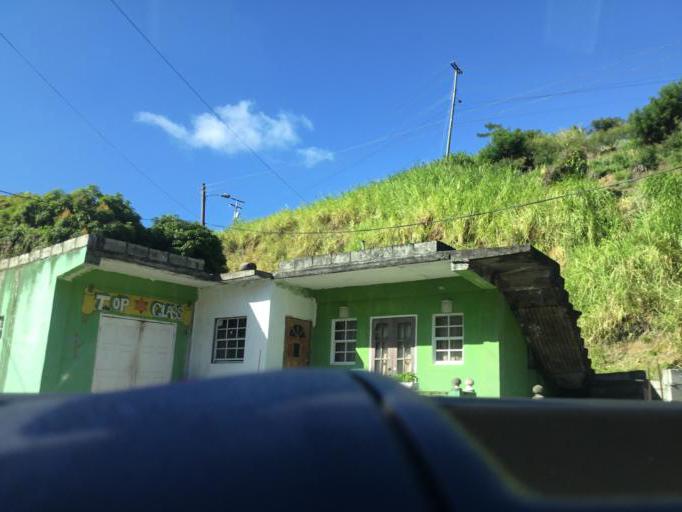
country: VC
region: Saint David
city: Chateaubelair
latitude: 13.2749
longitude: -61.2489
